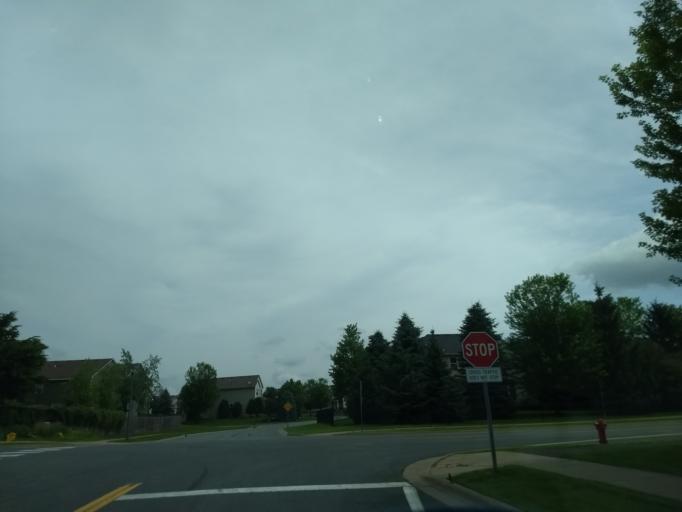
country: US
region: Minnesota
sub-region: Dakota County
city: Rosemount
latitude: 44.7444
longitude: -93.0973
